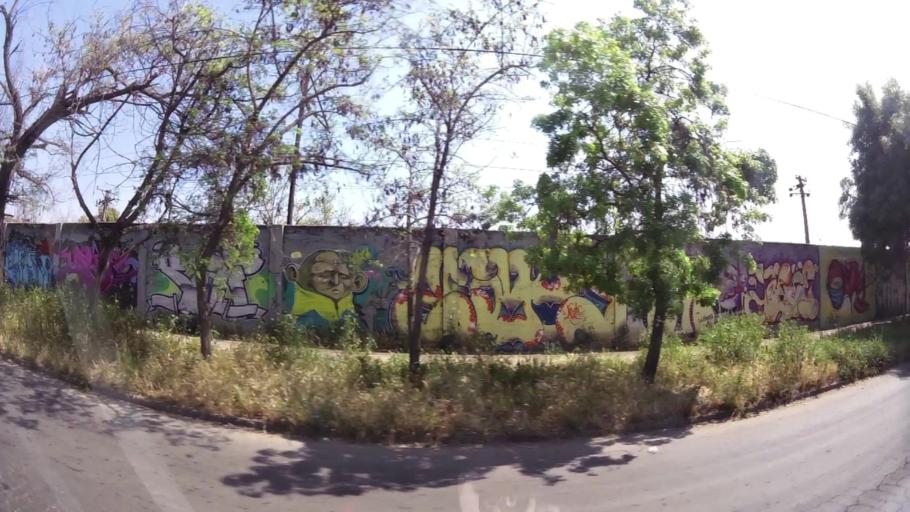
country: CL
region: Santiago Metropolitan
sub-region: Provincia de Santiago
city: Santiago
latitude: -33.4746
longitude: -70.6730
